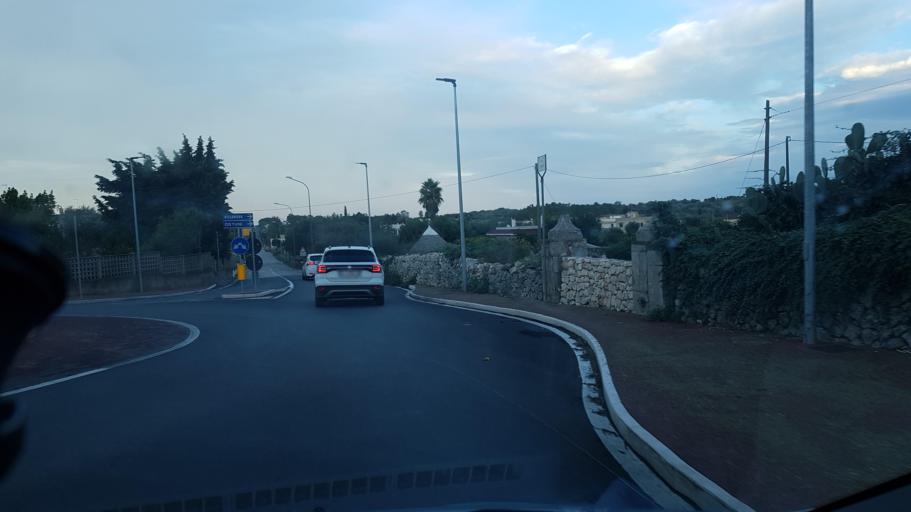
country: IT
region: Apulia
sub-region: Provincia di Brindisi
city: Ceglie Messapica
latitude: 40.6493
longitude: 17.5223
